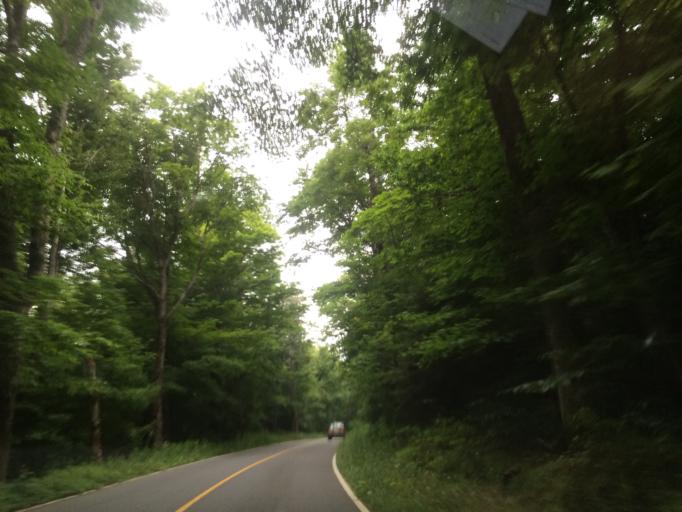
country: US
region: Massachusetts
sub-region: Berkshire County
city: Adams
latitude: 42.6151
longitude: -73.2001
